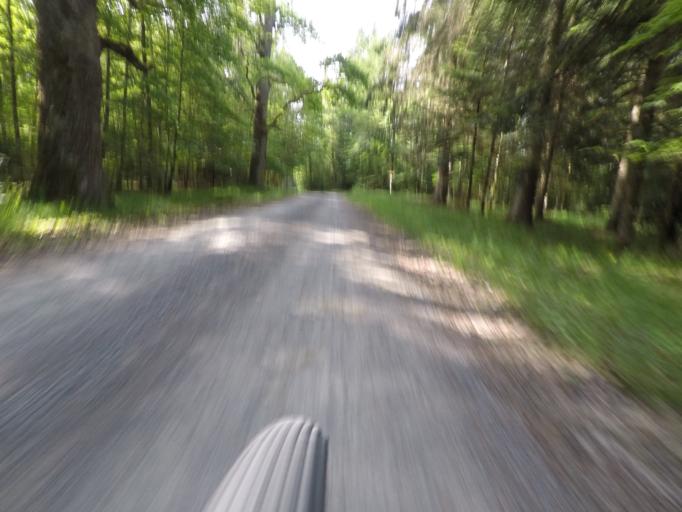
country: DE
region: Baden-Wuerttemberg
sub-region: Regierungsbezirk Stuttgart
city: Weil im Schonbuch
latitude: 48.5784
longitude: 9.0594
